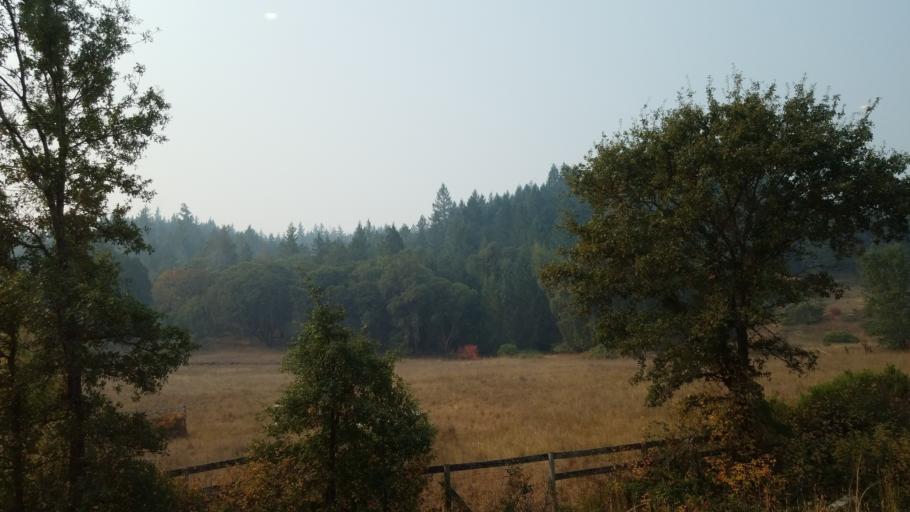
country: US
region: California
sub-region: Mendocino County
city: Willits
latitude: 39.4039
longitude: -123.3727
